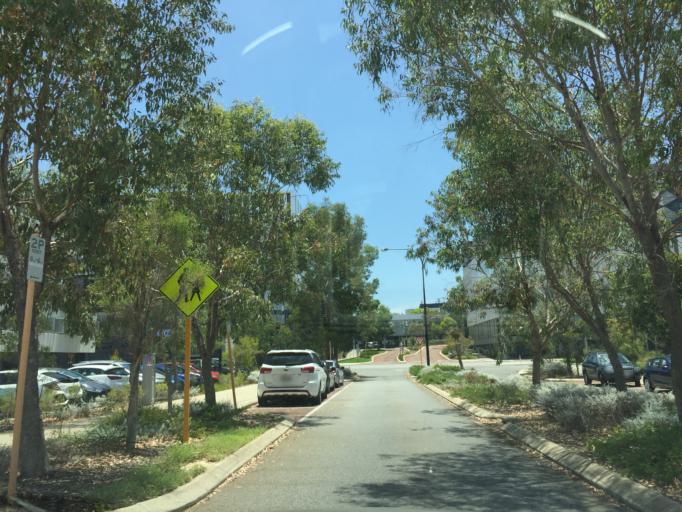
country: AU
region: Western Australia
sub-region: Melville
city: Winthrop
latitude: -32.0719
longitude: 115.8450
